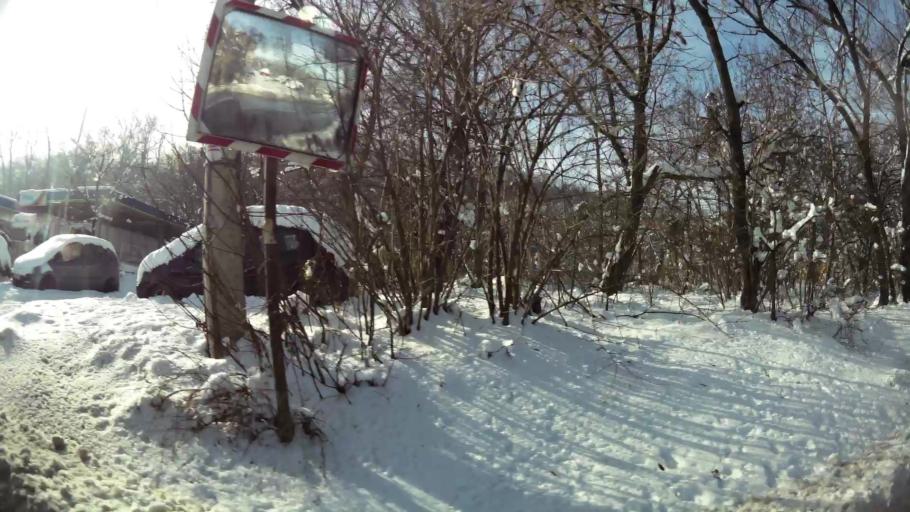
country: RS
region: Central Serbia
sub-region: Belgrade
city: Palilula
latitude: 44.8089
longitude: 20.5128
